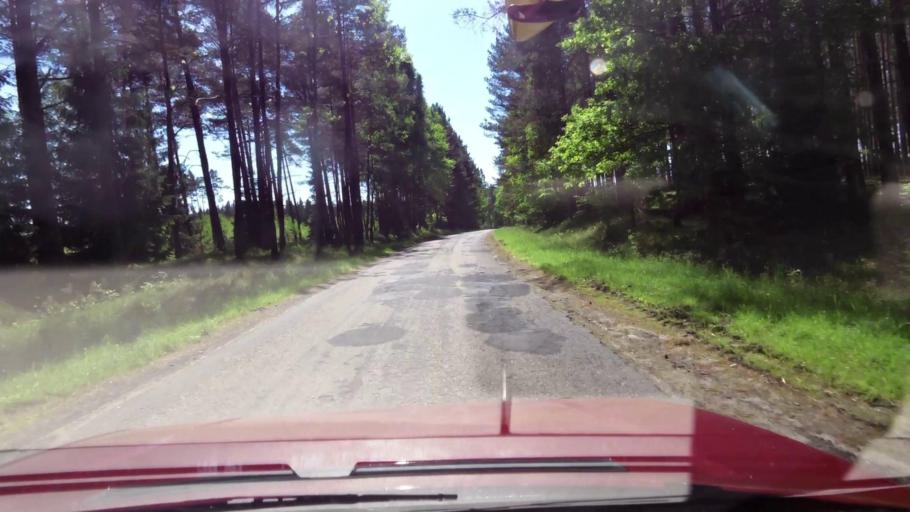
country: PL
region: West Pomeranian Voivodeship
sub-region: Powiat koszalinski
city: Bobolice
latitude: 54.0609
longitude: 16.5696
